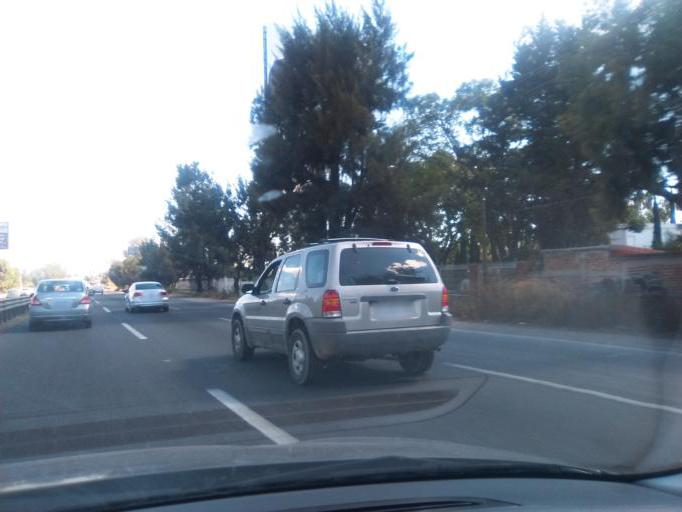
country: MX
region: Guanajuato
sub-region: Silao de la Victoria
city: El Refugio de los Sauces
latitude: 21.0290
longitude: -101.5446
